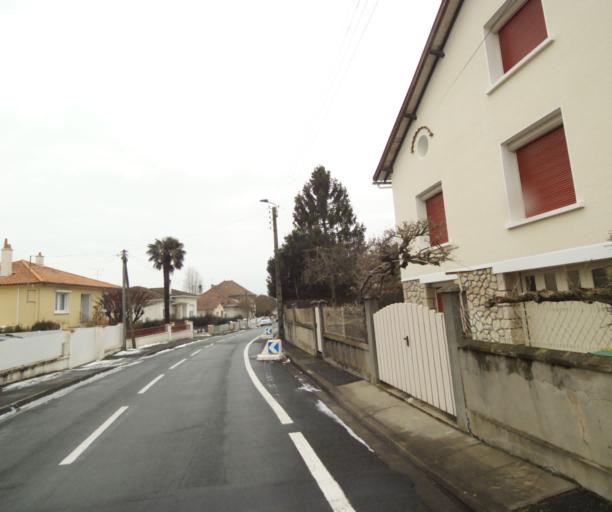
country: FR
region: Poitou-Charentes
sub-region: Departement des Deux-Sevres
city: Niort
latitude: 46.3178
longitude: -0.4745
